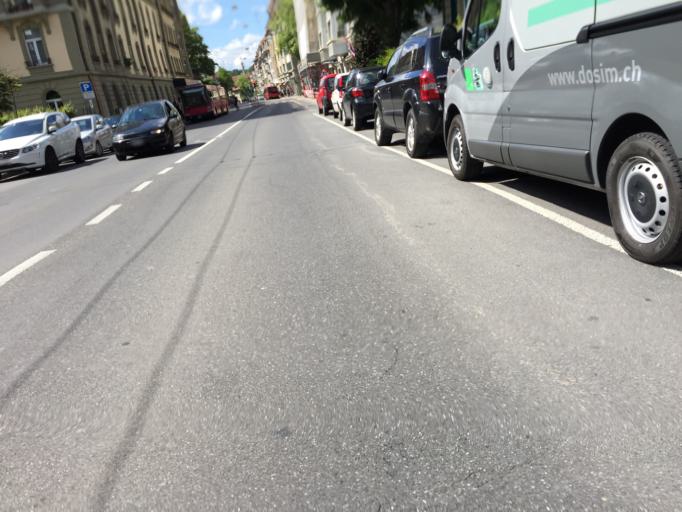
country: CH
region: Bern
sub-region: Bern-Mittelland District
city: Bern
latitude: 46.9525
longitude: 7.4336
